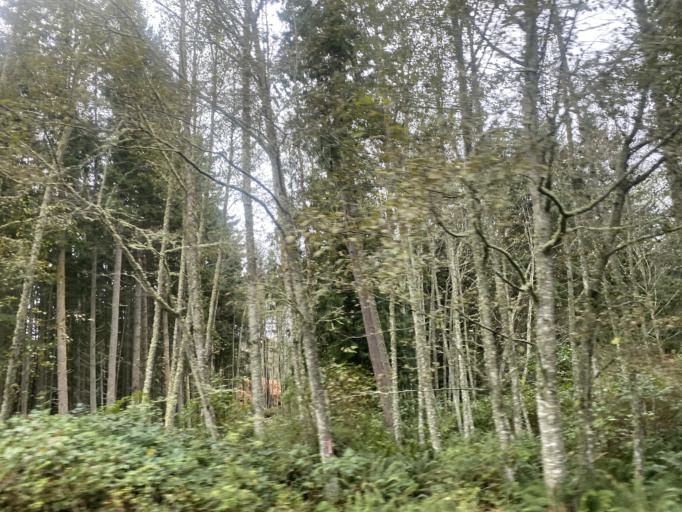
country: US
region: Washington
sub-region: Island County
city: Freeland
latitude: 48.0764
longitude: -122.5670
